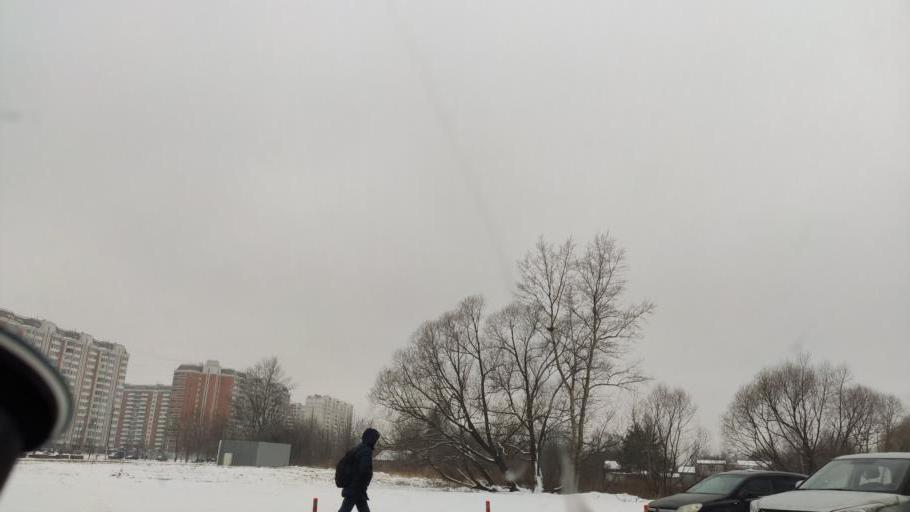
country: RU
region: Moskovskaya
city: Shcherbinka
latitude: 55.5058
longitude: 37.5857
